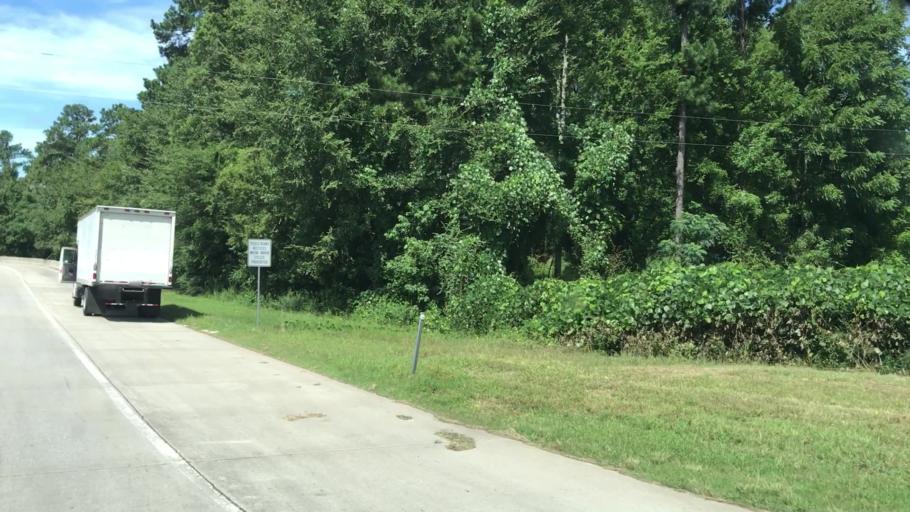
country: US
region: Georgia
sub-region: Taliaferro County
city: Crawfordville
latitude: 33.5008
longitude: -82.8057
